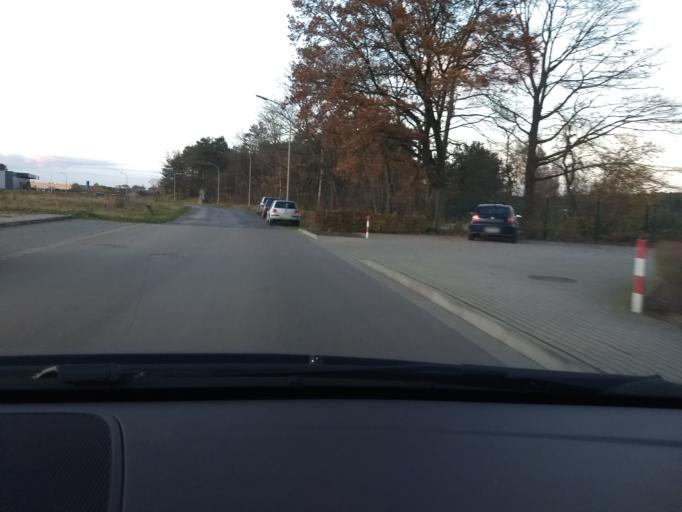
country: DE
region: North Rhine-Westphalia
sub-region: Regierungsbezirk Munster
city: Borken
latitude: 51.8503
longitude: 6.8948
